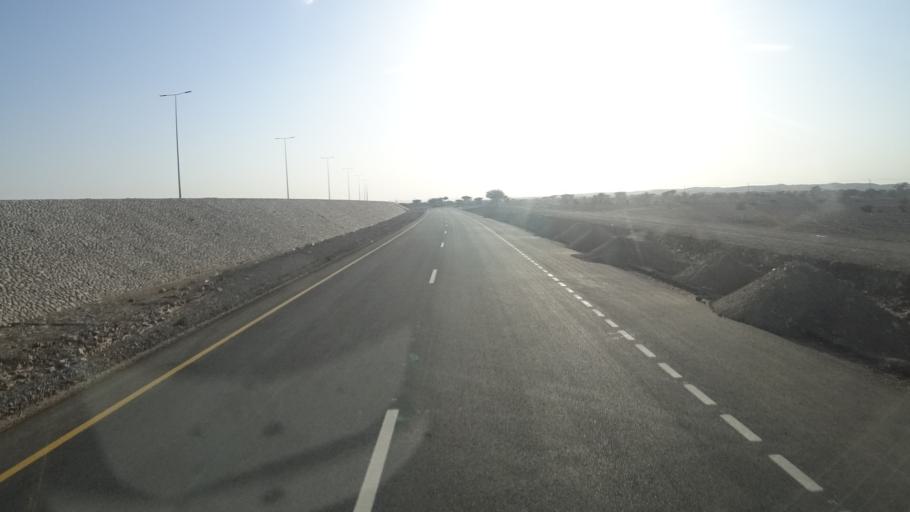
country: OM
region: Ash Sharqiyah
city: Badiyah
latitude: 22.4922
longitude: 58.9288
